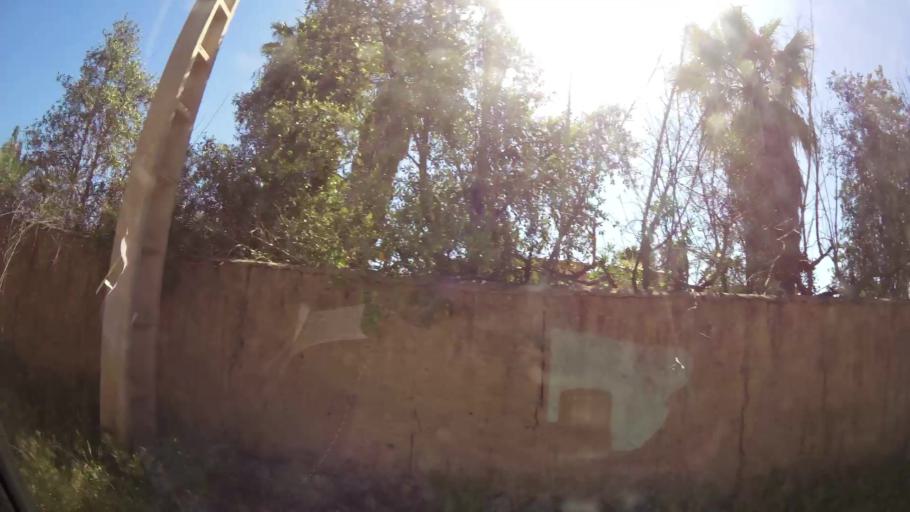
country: MA
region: Marrakech-Tensift-Al Haouz
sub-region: Marrakech
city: Marrakesh
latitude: 31.6638
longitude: -7.9580
